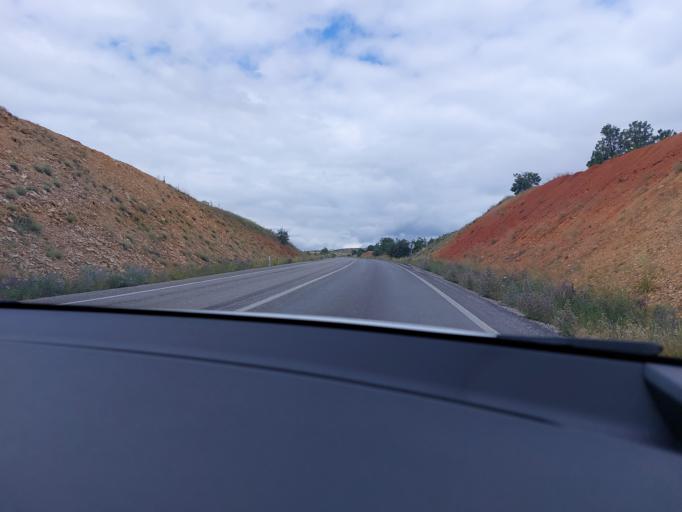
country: TR
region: Konya
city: Doganbey
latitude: 37.8951
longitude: 31.7966
